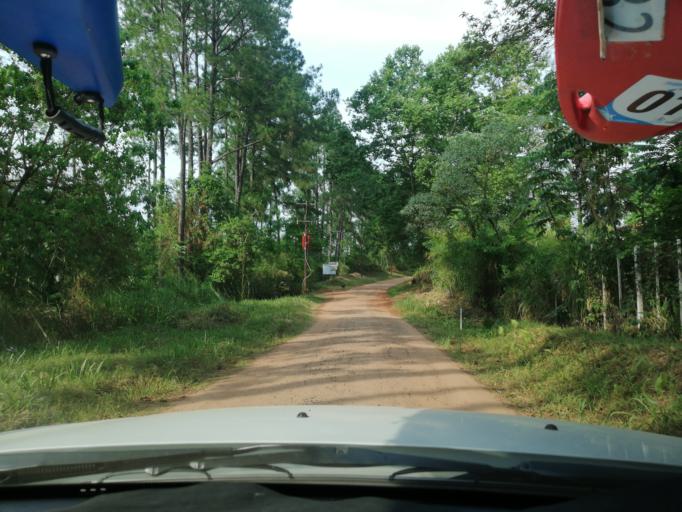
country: AR
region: Misiones
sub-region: Departamento de San Ignacio
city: San Ignacio
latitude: -27.2924
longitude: -55.5638
